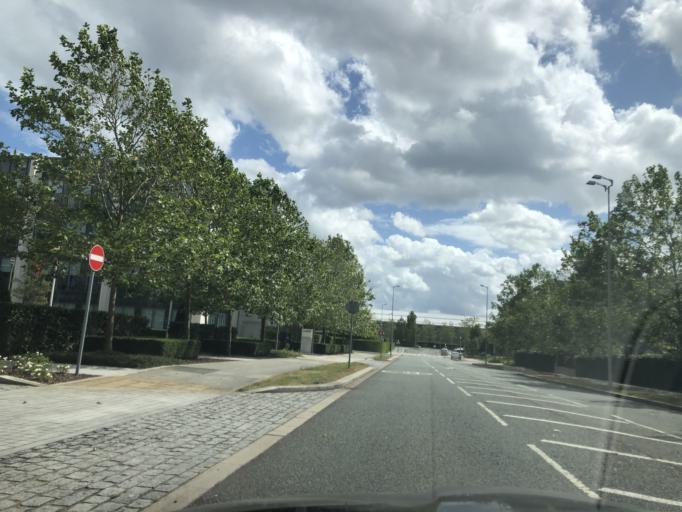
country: GB
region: England
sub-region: Hampshire
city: Farnborough
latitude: 51.2863
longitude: -0.7620
